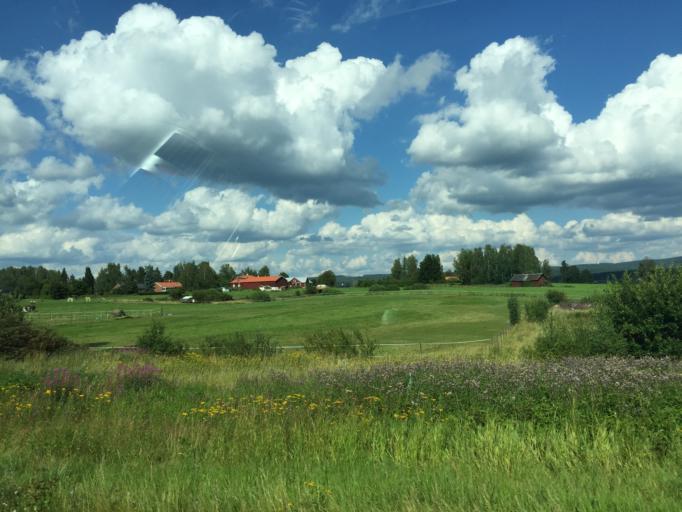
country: SE
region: Gaevleborg
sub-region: Bollnas Kommun
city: Bollnas
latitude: 61.3338
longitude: 16.4053
